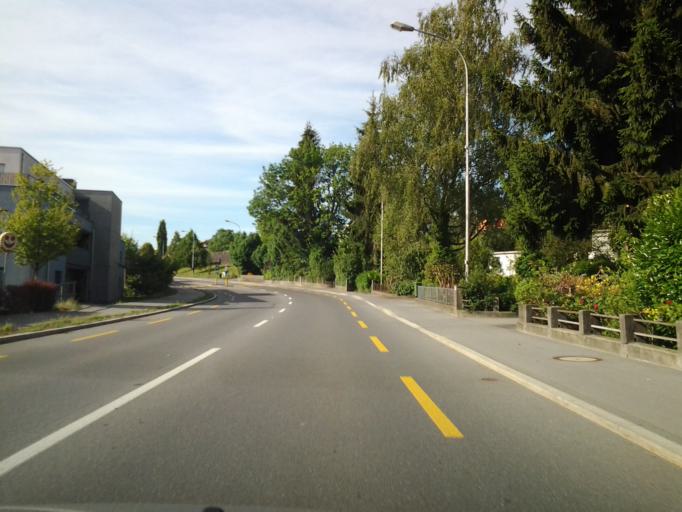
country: CH
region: Zug
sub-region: Zug
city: Cham
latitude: 47.1735
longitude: 8.4489
